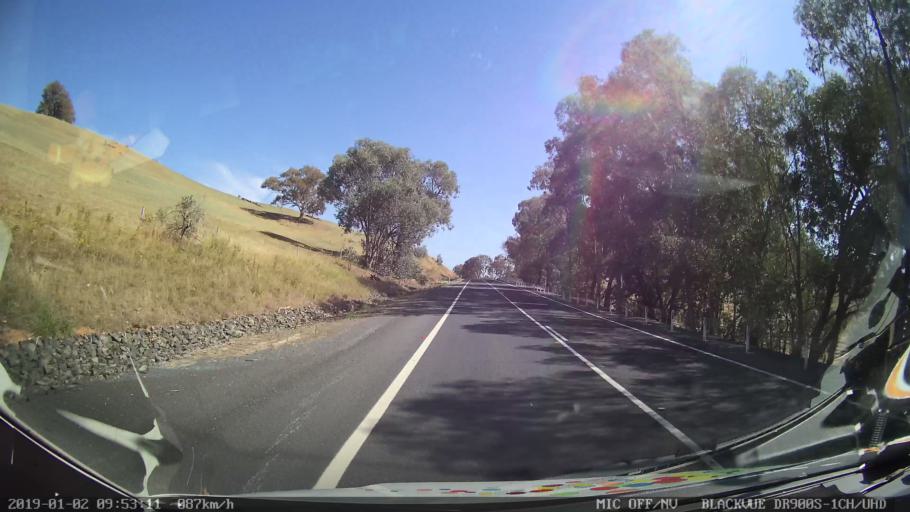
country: AU
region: New South Wales
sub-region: Tumut Shire
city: Tumut
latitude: -35.2509
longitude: 148.2035
